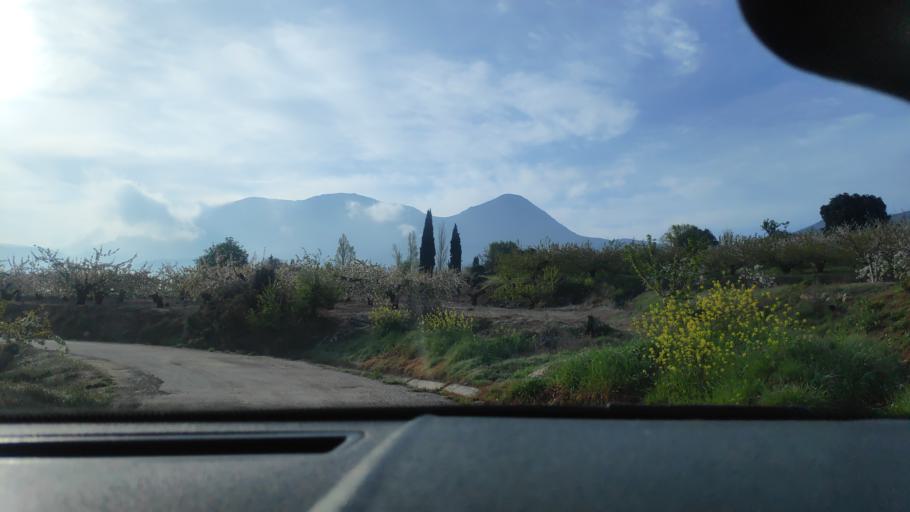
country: ES
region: Andalusia
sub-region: Provincia de Jaen
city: Torres
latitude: 37.7675
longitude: -3.5220
